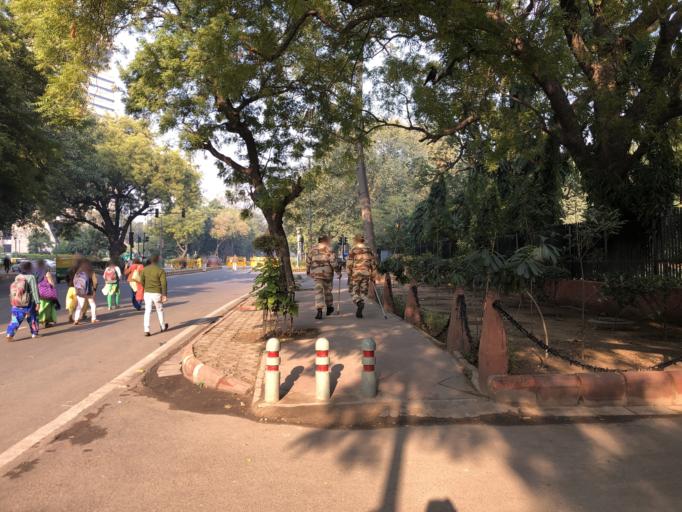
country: IN
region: NCT
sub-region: New Delhi
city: New Delhi
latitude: 28.6263
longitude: 77.2150
